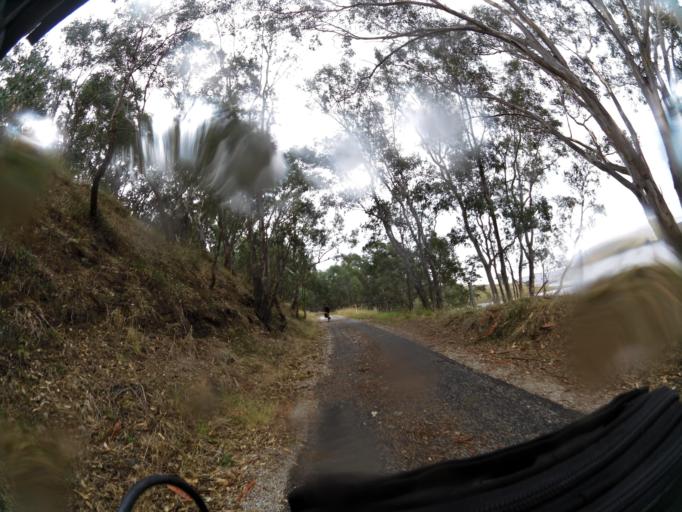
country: AU
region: New South Wales
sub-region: Albury Municipality
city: East Albury
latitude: -36.2147
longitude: 147.2399
